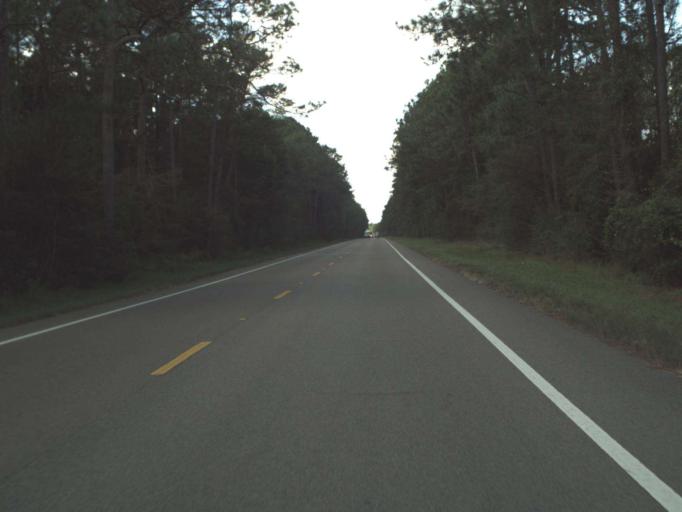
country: US
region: Florida
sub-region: Walton County
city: Freeport
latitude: 30.4655
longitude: -85.9415
